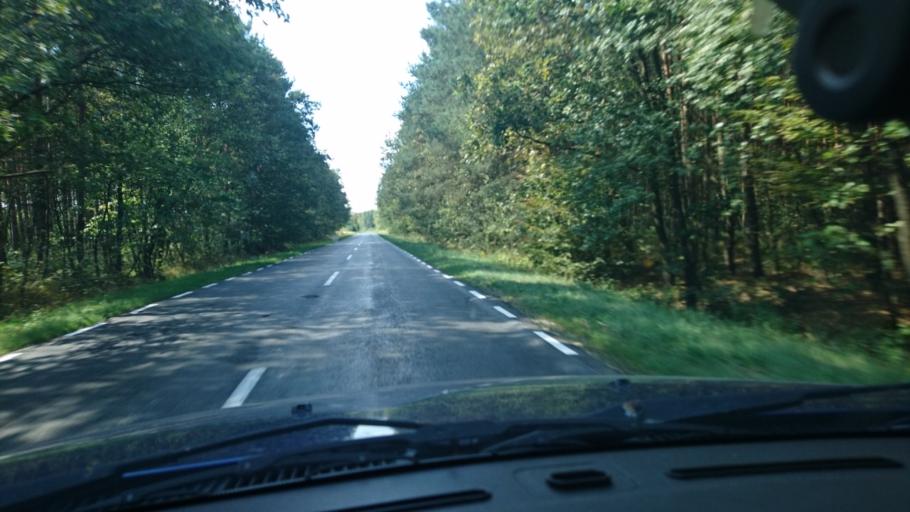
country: PL
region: Greater Poland Voivodeship
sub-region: Powiat krotoszynski
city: Sulmierzyce
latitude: 51.6000
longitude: 17.5968
